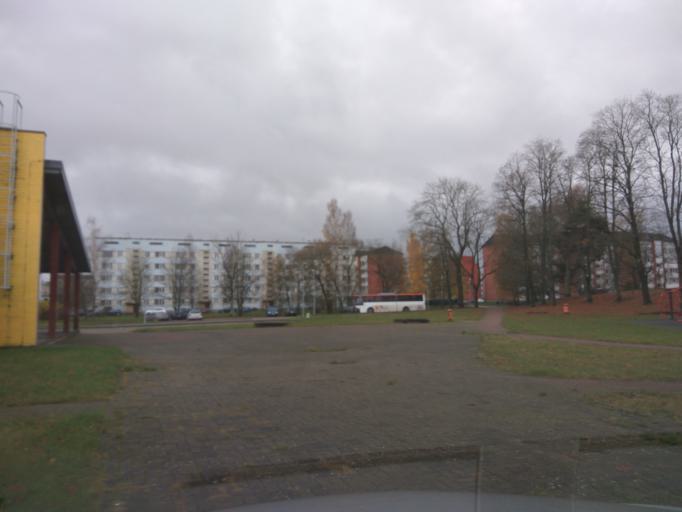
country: LV
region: Kuldigas Rajons
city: Kuldiga
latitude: 56.9759
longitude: 21.9535
